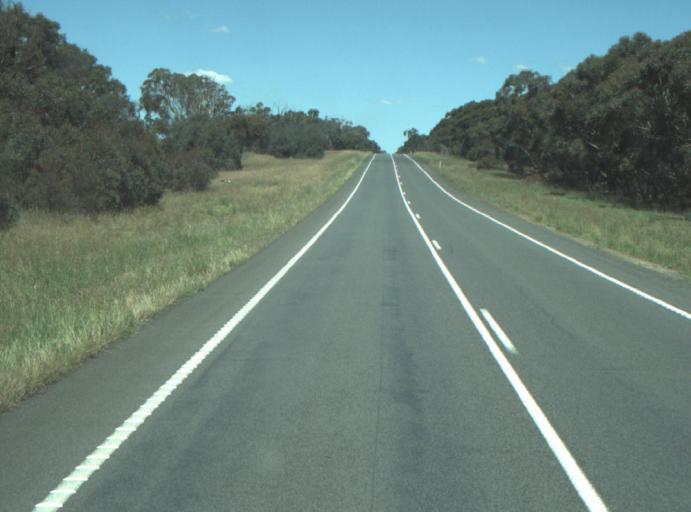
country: AU
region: Victoria
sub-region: Greater Geelong
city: Lara
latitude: -37.9114
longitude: 144.3681
